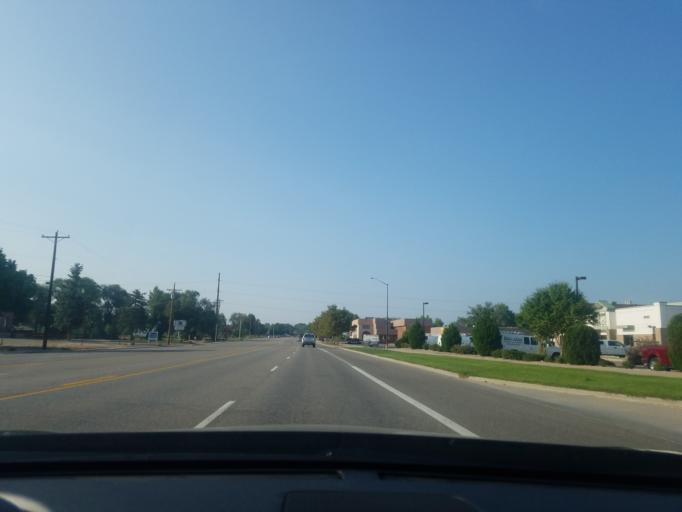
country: US
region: Colorado
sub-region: Larimer County
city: Loveland
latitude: 40.3800
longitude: -105.0732
